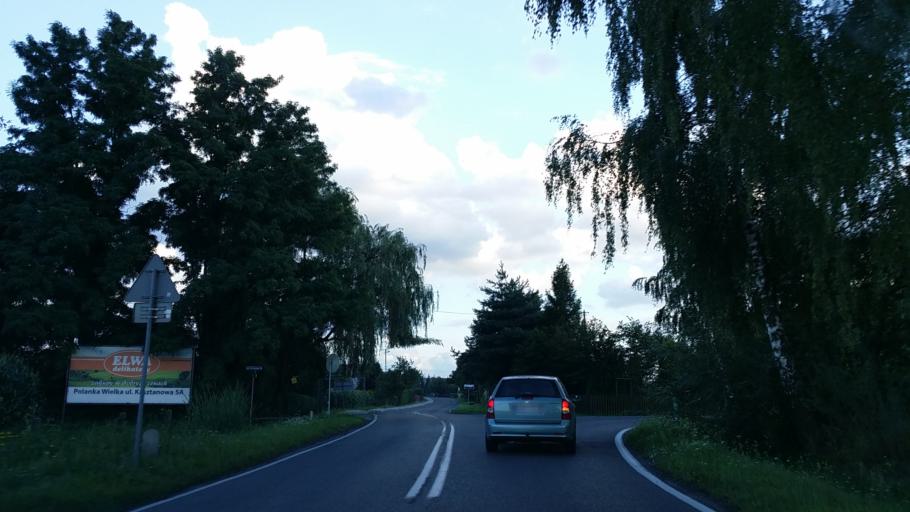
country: PL
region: Lesser Poland Voivodeship
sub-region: Powiat oswiecimski
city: Przeciszow
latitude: 49.9910
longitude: 19.3619
